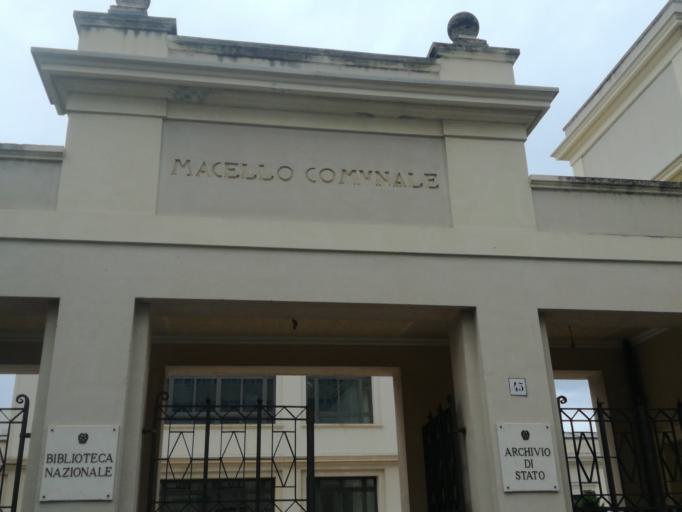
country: IT
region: Apulia
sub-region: Provincia di Bari
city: Bari
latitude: 41.1286
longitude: 16.8470
